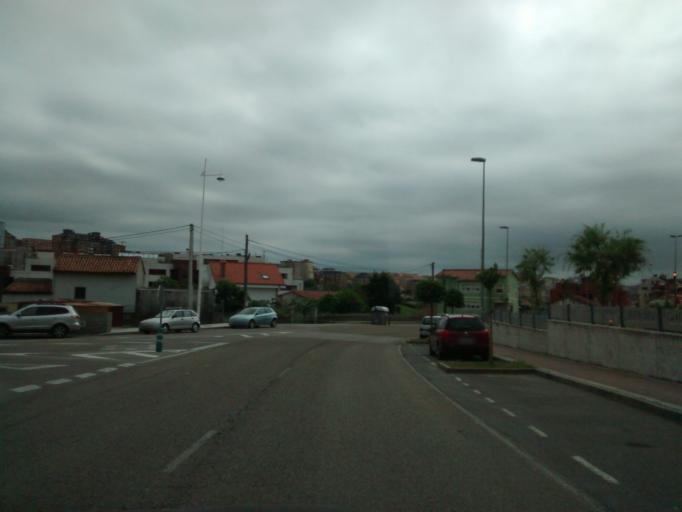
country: ES
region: Cantabria
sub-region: Provincia de Cantabria
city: Santander
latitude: 43.4728
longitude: -3.8179
